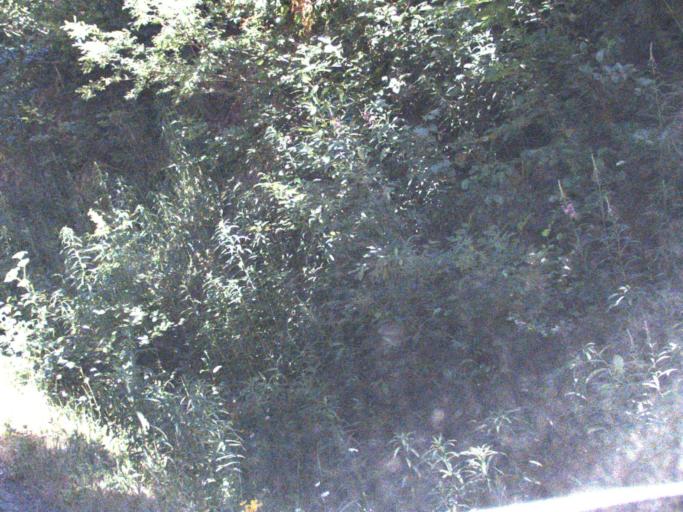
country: US
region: Washington
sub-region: King County
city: Enumclaw
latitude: 46.8341
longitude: -121.5342
